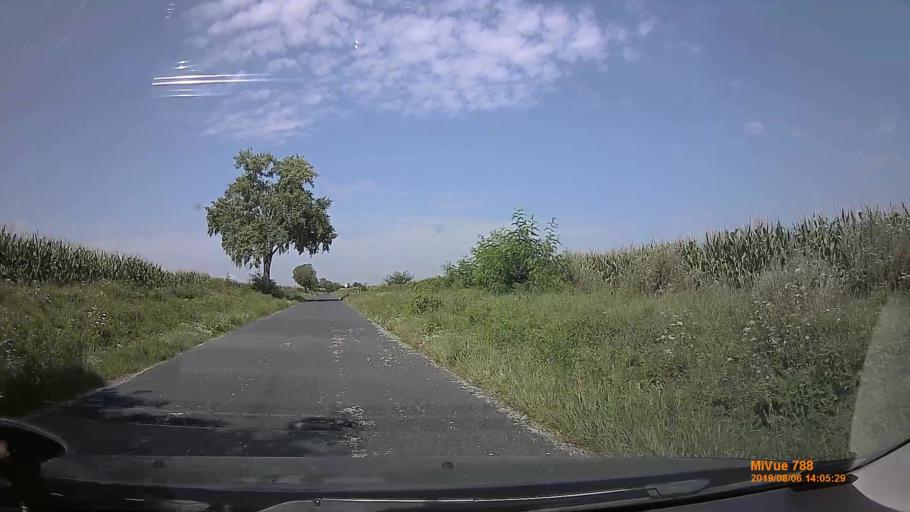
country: HU
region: Zala
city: Zalakomar
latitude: 46.5121
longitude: 17.0839
